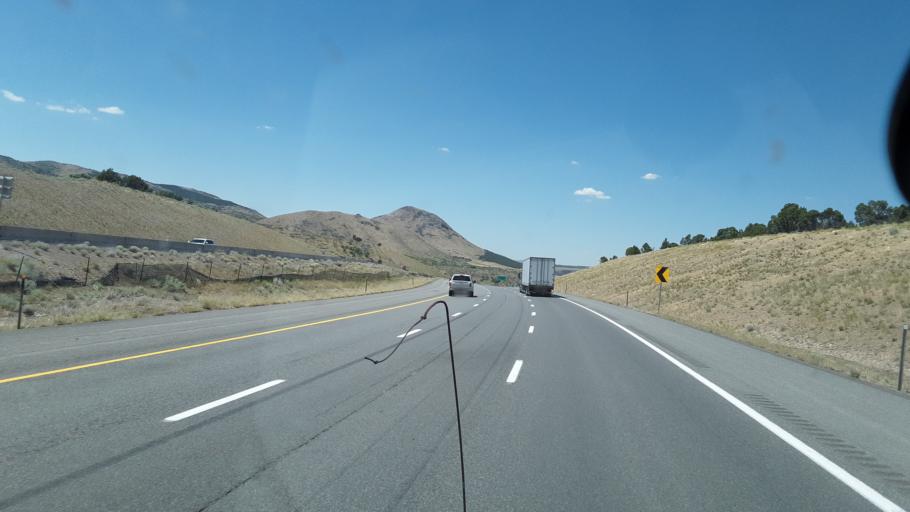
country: US
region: Utah
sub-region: Beaver County
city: Beaver
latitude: 38.4775
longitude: -112.6119
